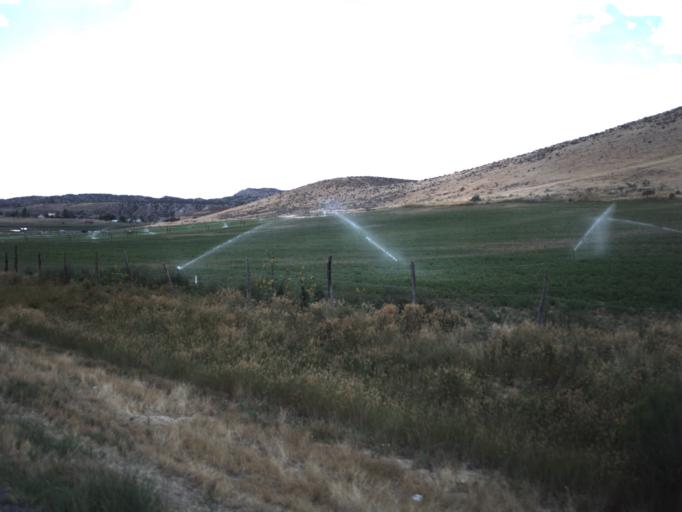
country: US
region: Utah
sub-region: Sanpete County
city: Gunnison
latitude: 39.1455
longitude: -111.7096
